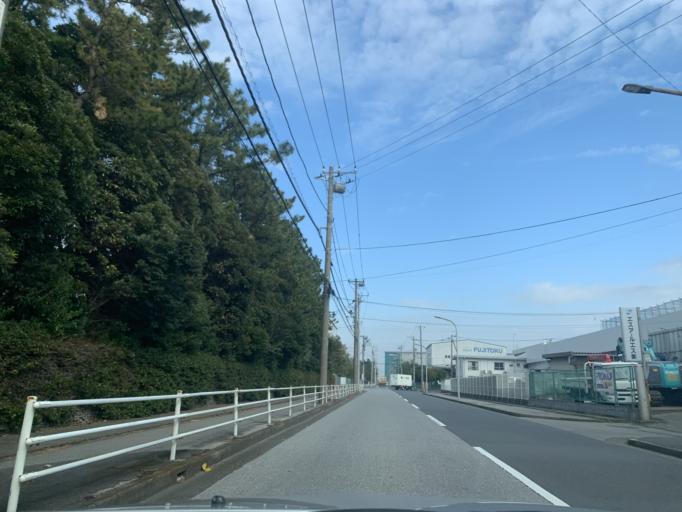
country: JP
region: Tokyo
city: Urayasu
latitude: 35.6661
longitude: 139.9257
